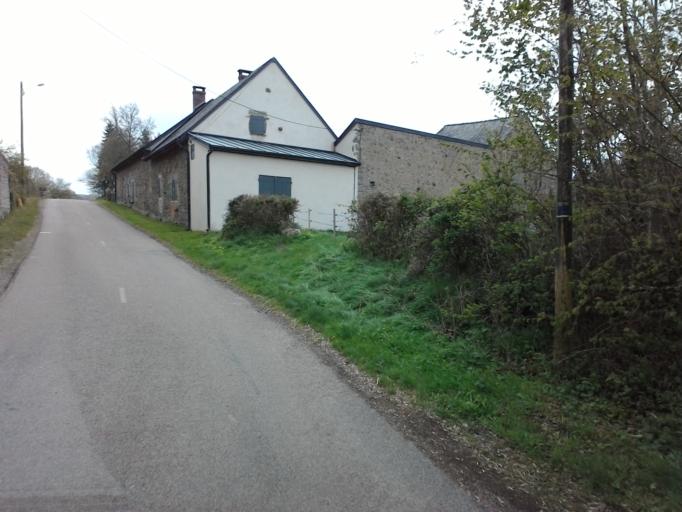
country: FR
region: Bourgogne
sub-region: Departement de la Cote-d'Or
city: Saulieu
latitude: 47.2430
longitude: 4.1999
